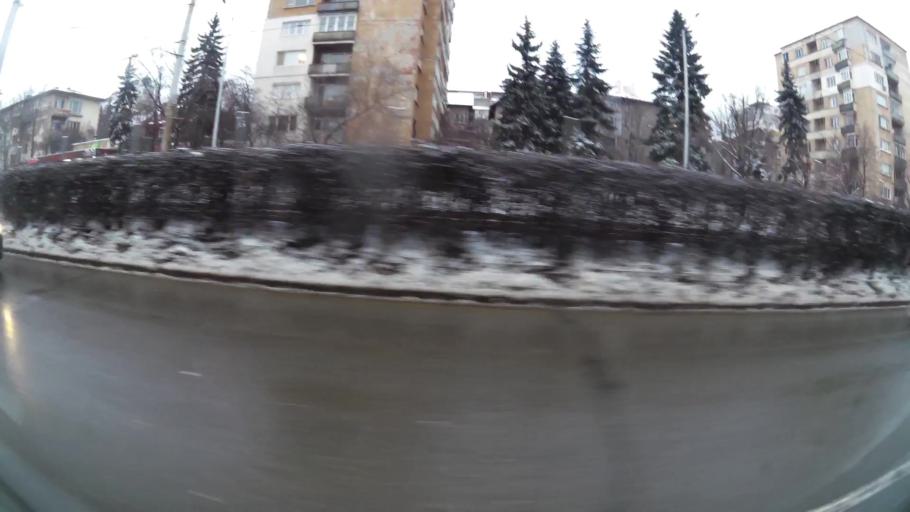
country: BG
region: Sofia-Capital
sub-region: Stolichna Obshtina
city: Sofia
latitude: 42.6886
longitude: 23.3528
